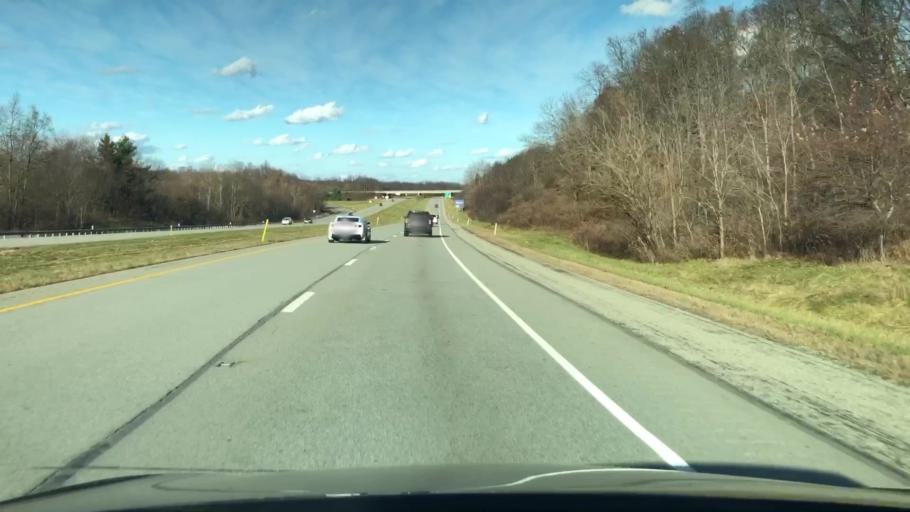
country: US
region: Pennsylvania
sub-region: Armstrong County
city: Freeport
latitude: 40.6839
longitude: -79.7132
